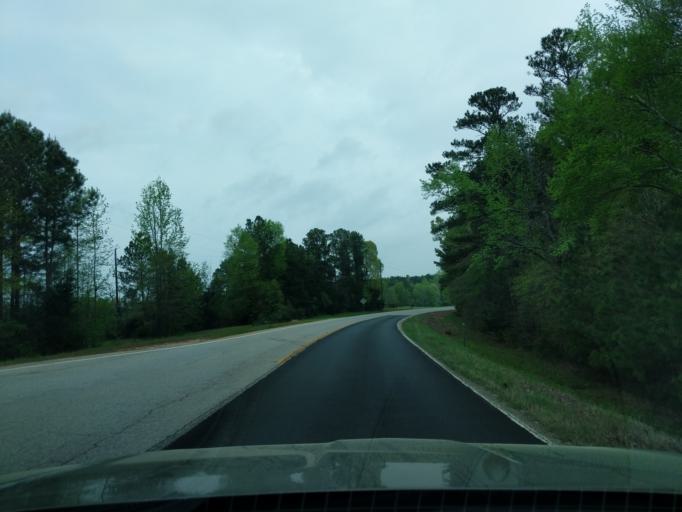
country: US
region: Georgia
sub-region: Lincoln County
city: Lincolnton
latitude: 33.7803
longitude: -82.3815
